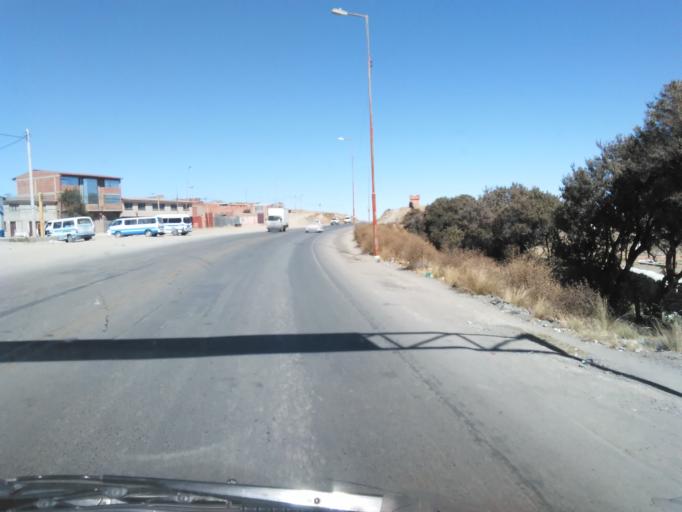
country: BO
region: Oruro
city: Oruro
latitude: -17.9812
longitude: -67.0501
